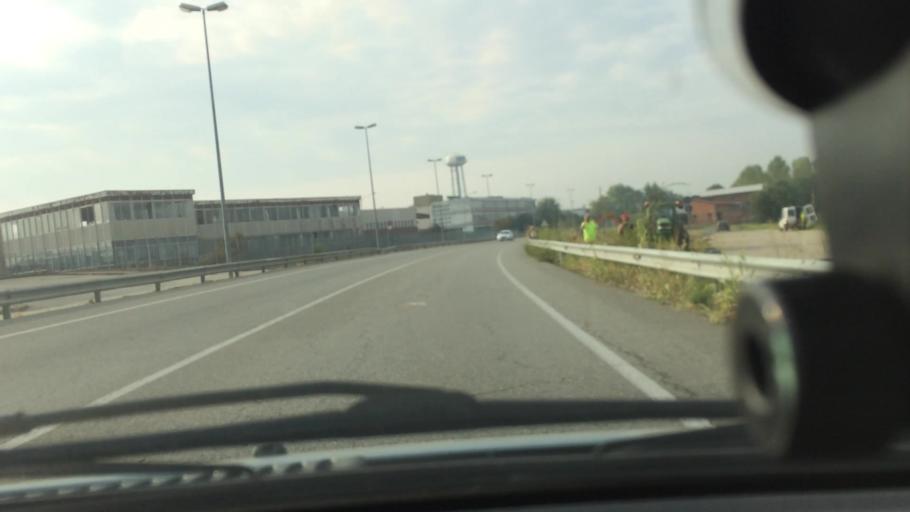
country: IT
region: Piedmont
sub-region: Provincia di Torino
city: Villastellone
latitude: 44.9151
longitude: 7.7430
